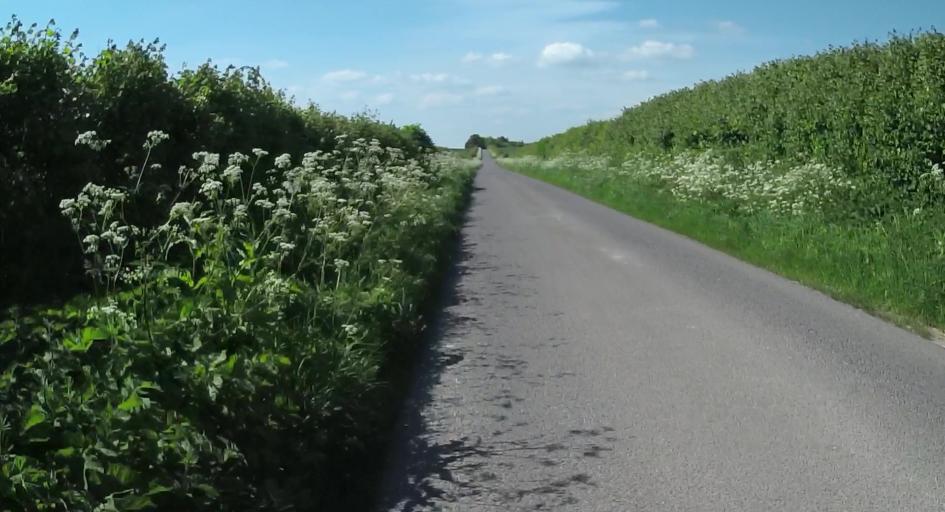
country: GB
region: England
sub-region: Hampshire
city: Kings Worthy
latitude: 51.0752
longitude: -1.2800
